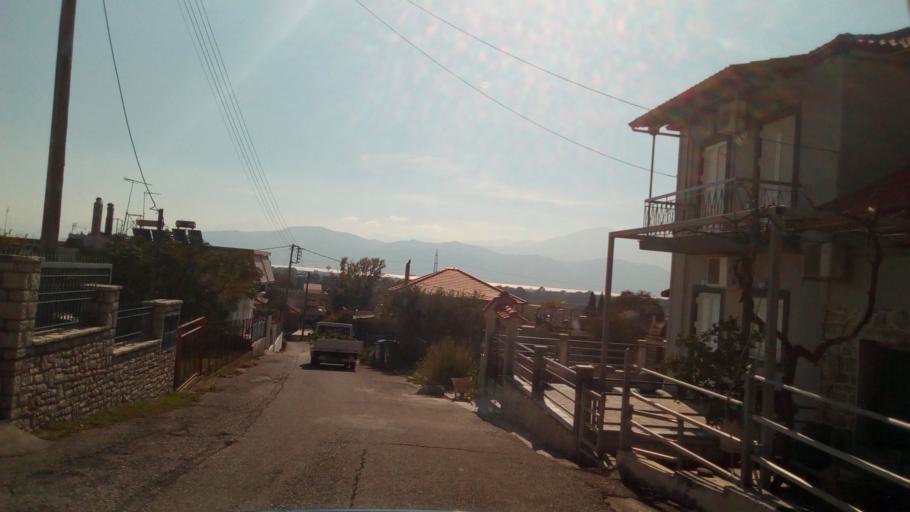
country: GR
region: West Greece
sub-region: Nomos Aitolias kai Akarnanias
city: Nafpaktos
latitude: 38.4157
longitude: 21.8743
